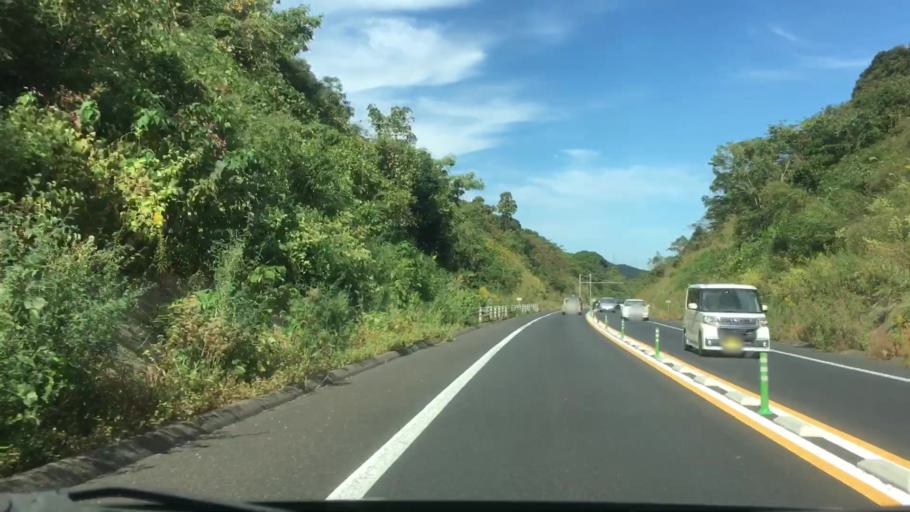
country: JP
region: Nagasaki
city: Sasebo
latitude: 33.1915
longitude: 129.6833
